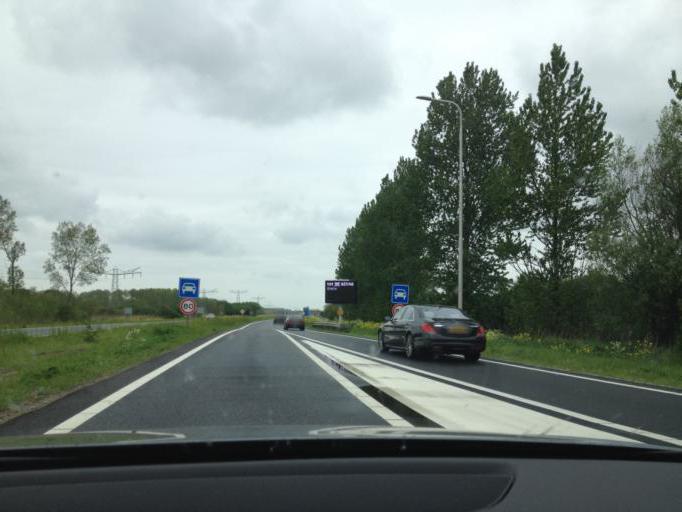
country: NL
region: Utrecht
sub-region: Gemeente Bunschoten
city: Spakenburg
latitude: 52.3095
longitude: 5.3453
